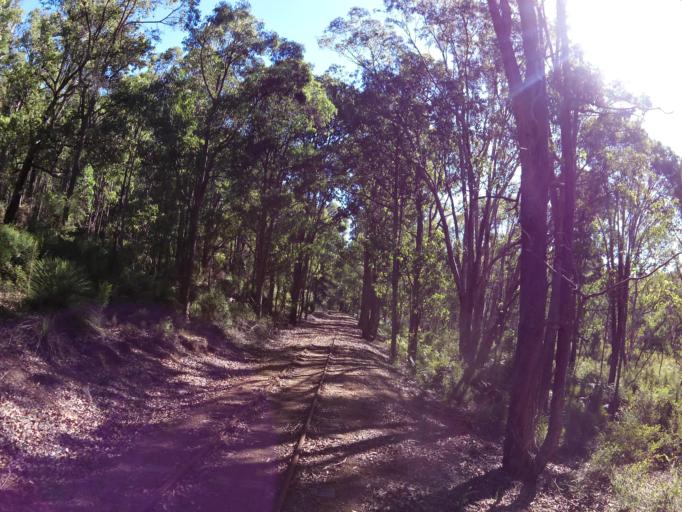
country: AU
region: Western Australia
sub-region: Waroona
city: Waroona
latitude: -32.7103
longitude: 116.0825
